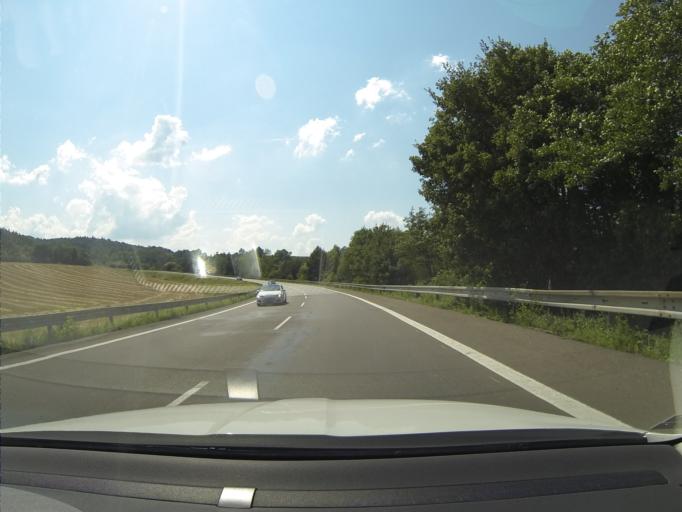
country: SK
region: Nitriansky
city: Prievidza
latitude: 48.7825
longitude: 18.6787
